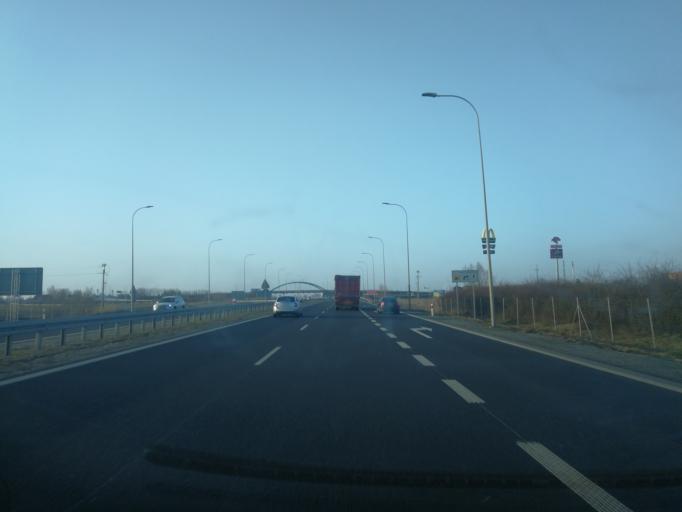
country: PL
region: Pomeranian Voivodeship
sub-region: Powiat nowodworski
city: Nowy Dwor Gdanski
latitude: 54.2089
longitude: 19.1067
